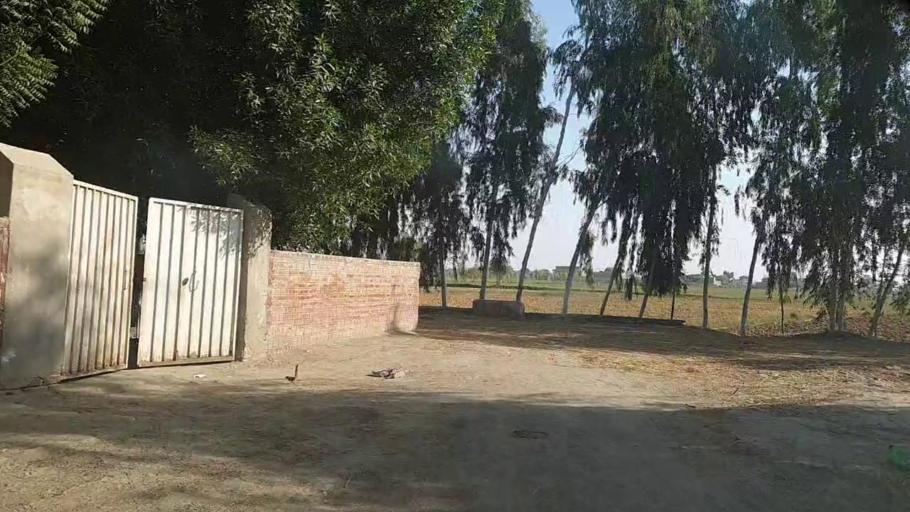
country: PK
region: Sindh
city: Tangwani
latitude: 28.2843
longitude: 69.0019
